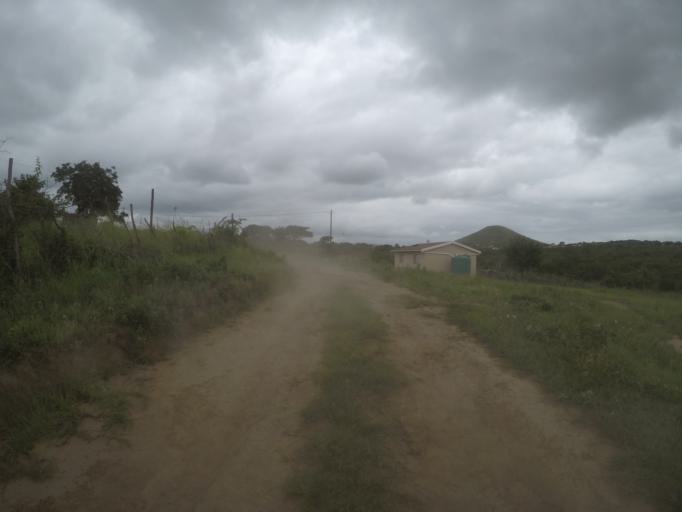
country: ZA
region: KwaZulu-Natal
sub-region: uThungulu District Municipality
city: Empangeni
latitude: -28.5938
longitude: 31.8438
